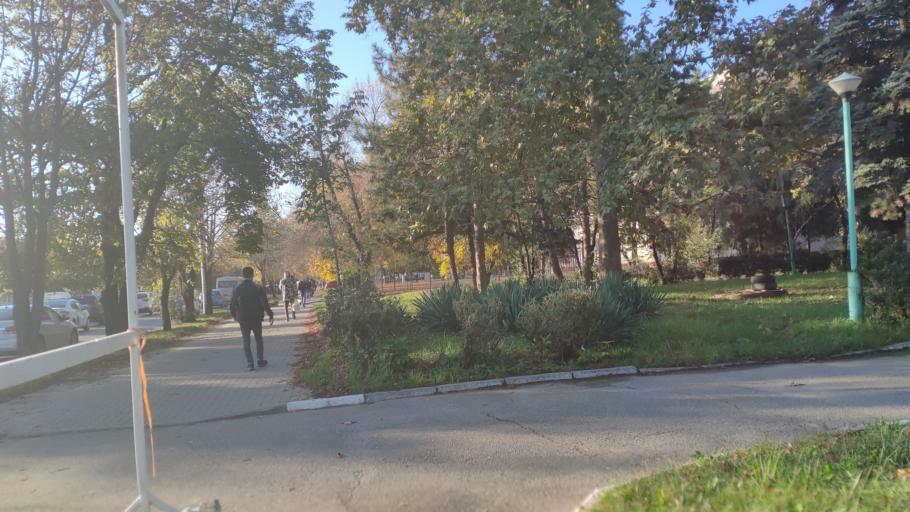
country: RU
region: Krasnodarskiy
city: Krasnodar
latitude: 45.0763
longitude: 39.0007
